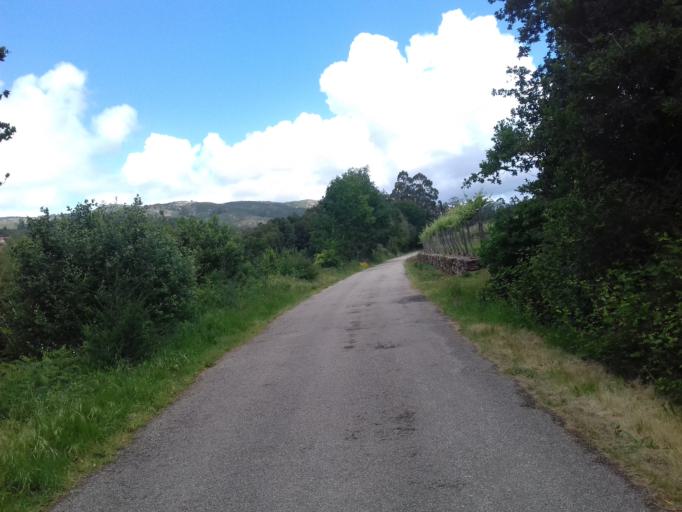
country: ES
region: Galicia
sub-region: Provincia de Pontevedra
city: O Rosal
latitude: 41.9432
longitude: -8.8258
